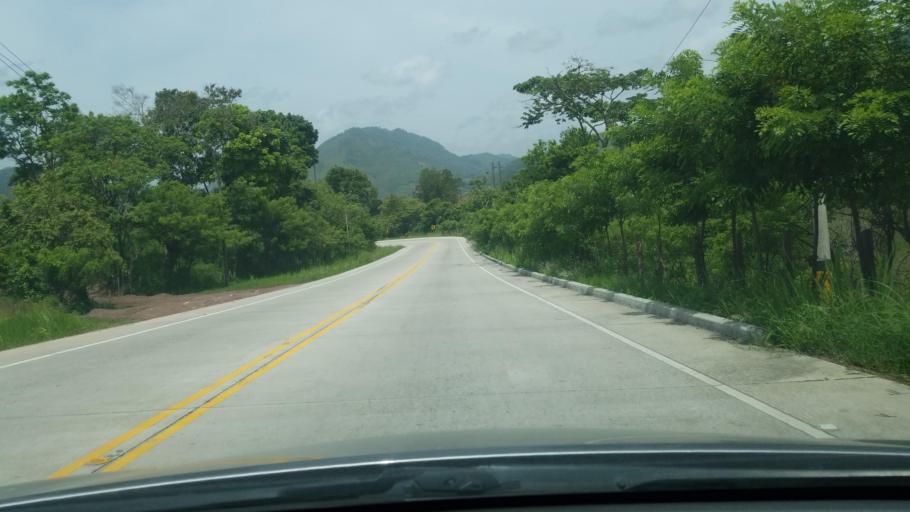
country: HN
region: Copan
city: Quezailica
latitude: 14.9014
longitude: -88.7557
